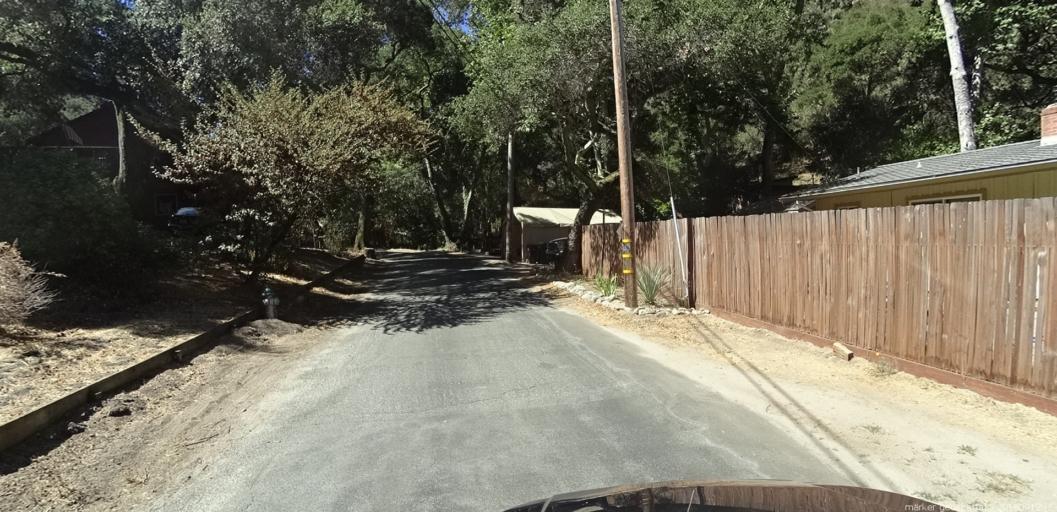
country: US
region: California
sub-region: Monterey County
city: Carmel Valley Village
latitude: 36.4634
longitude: -121.7251
